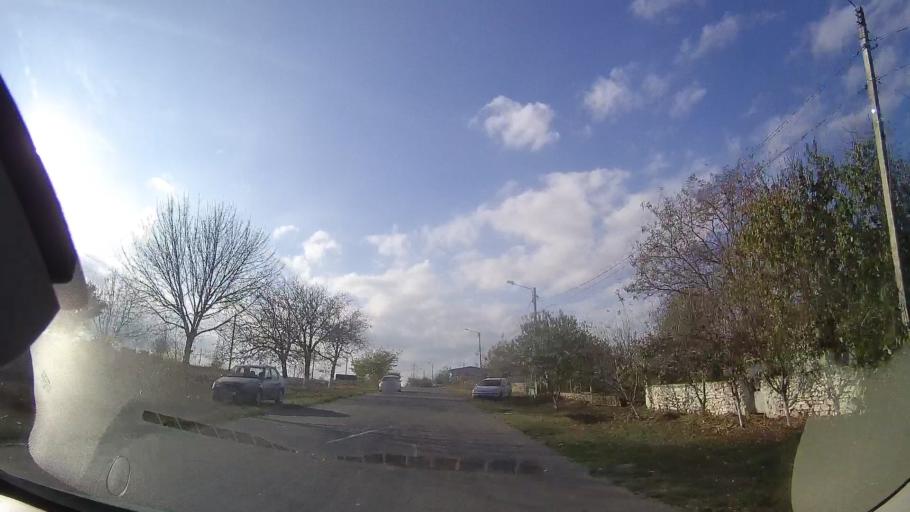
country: RO
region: Constanta
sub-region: Comuna Limanu
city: Limanu
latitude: 43.7944
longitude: 28.5272
